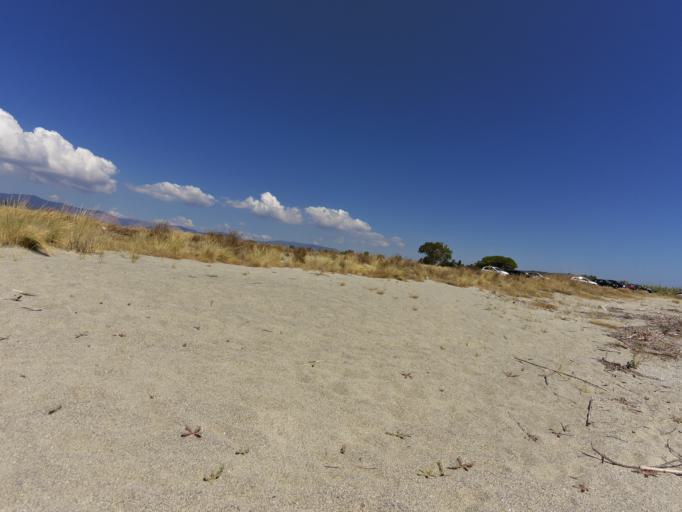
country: IT
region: Calabria
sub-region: Provincia di Reggio Calabria
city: Monasterace Marina
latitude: 38.4211
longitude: 16.5655
